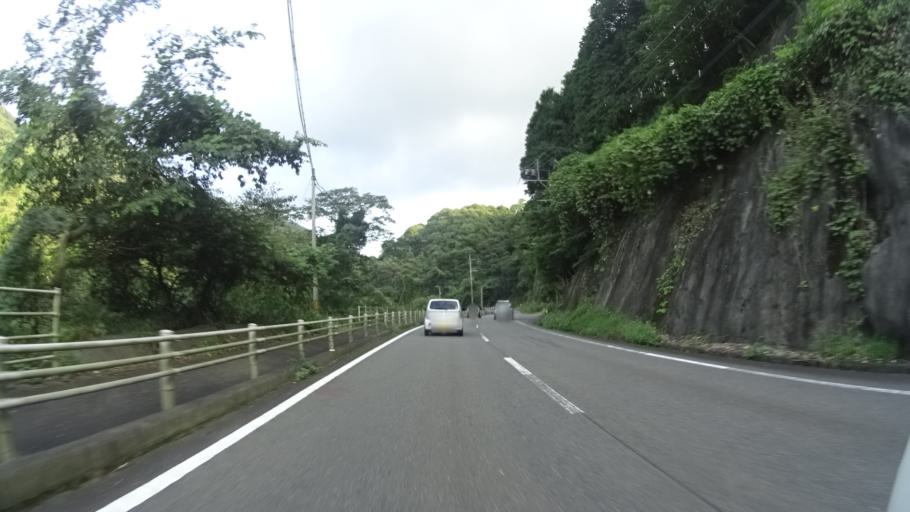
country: JP
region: Oita
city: Beppu
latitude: 33.3575
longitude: 131.3962
